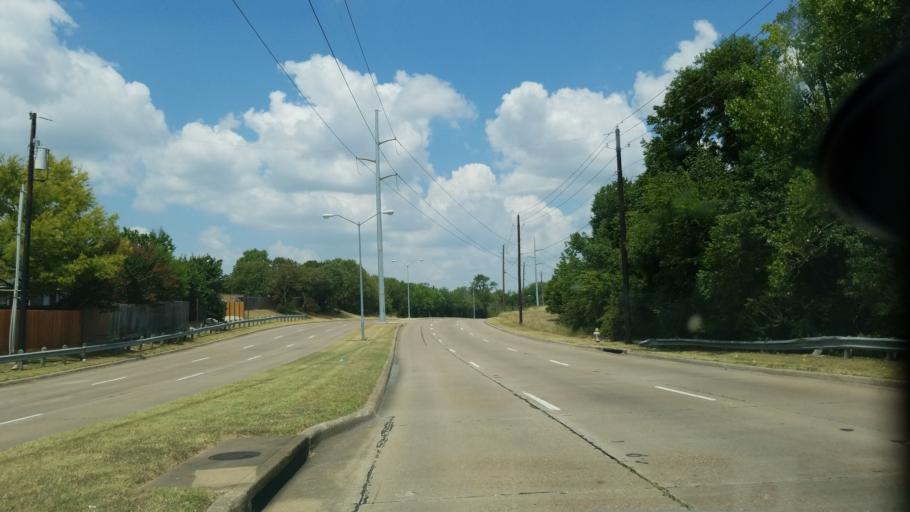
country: US
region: Texas
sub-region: Dallas County
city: Duncanville
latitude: 32.6710
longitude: -96.8820
